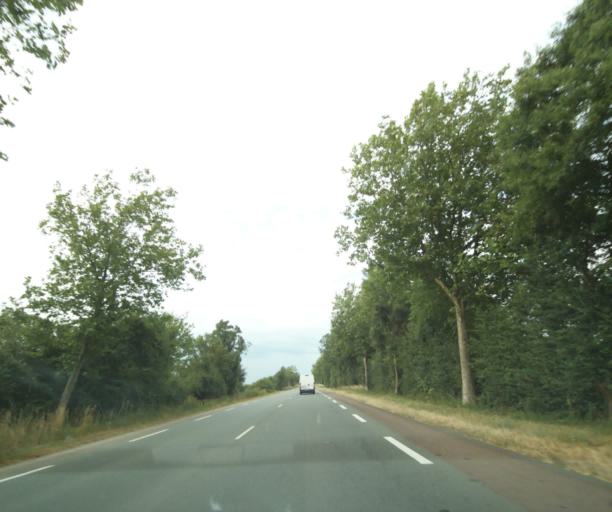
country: FR
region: Poitou-Charentes
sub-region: Departement de la Charente-Maritime
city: Marans
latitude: 46.2783
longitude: -0.9981
